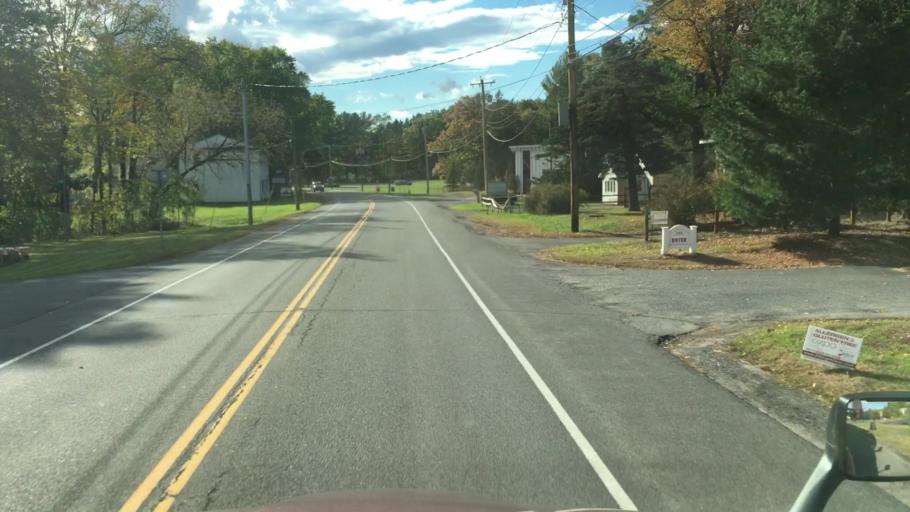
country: US
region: New York
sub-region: Schenectady County
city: East Glenville
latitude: 42.8958
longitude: -73.9153
